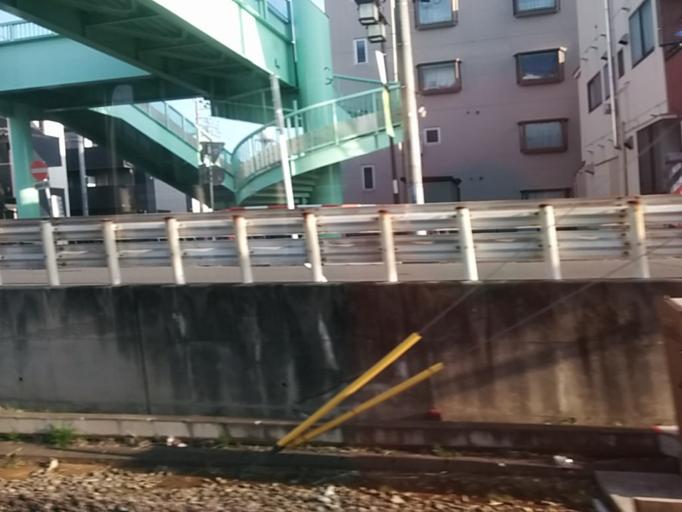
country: JP
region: Saitama
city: Oi
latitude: 35.8397
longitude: 139.5487
